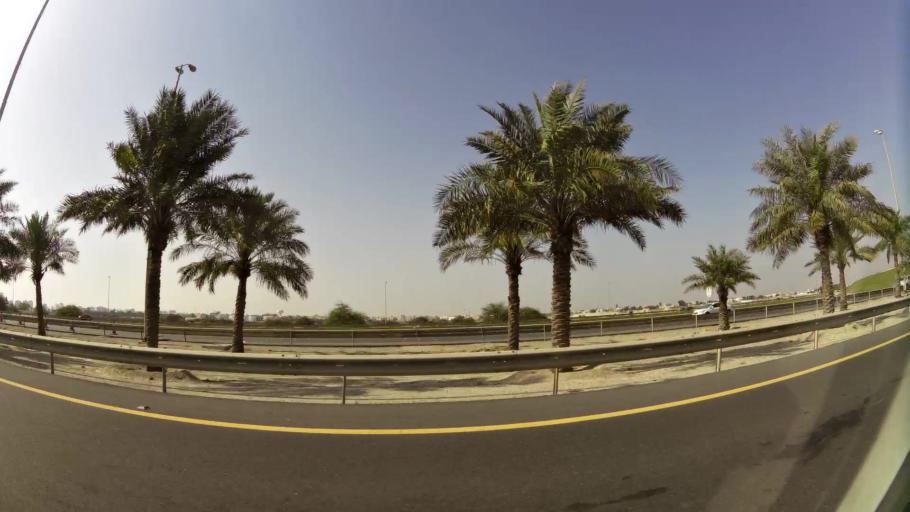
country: BH
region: Northern
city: Madinat `Isa
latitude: 26.1833
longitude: 50.4999
